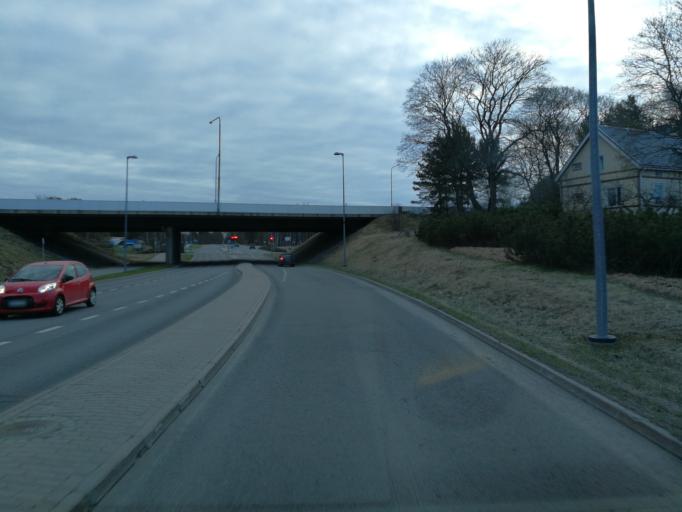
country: FI
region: Varsinais-Suomi
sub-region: Turku
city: Turku
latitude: 60.4259
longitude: 22.3107
